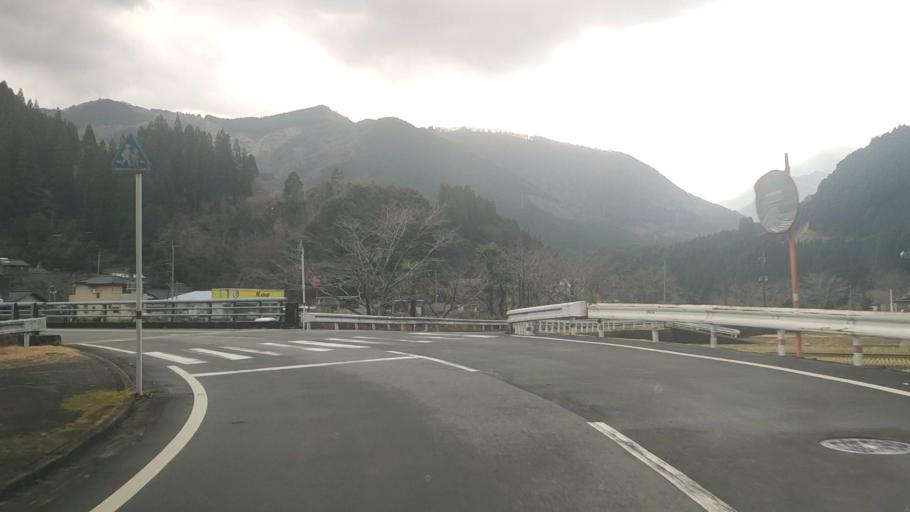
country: JP
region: Kumamoto
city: Hitoyoshi
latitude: 32.4415
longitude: 130.8563
